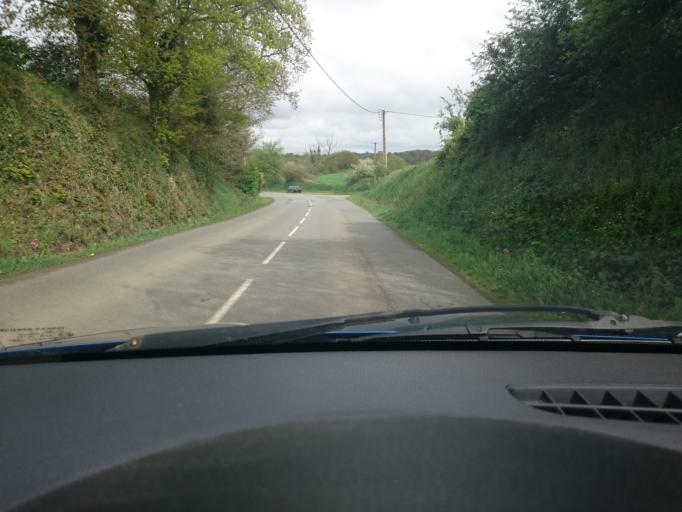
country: FR
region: Brittany
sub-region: Departement du Finistere
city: Plouvien
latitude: 48.5346
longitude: -4.4309
